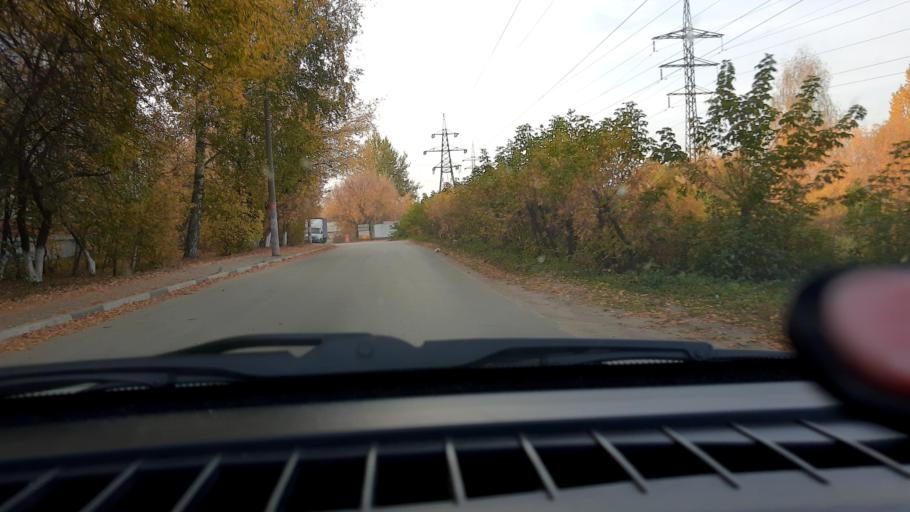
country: RU
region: Nizjnij Novgorod
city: Nizhniy Novgorod
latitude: 56.3114
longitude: 43.8804
